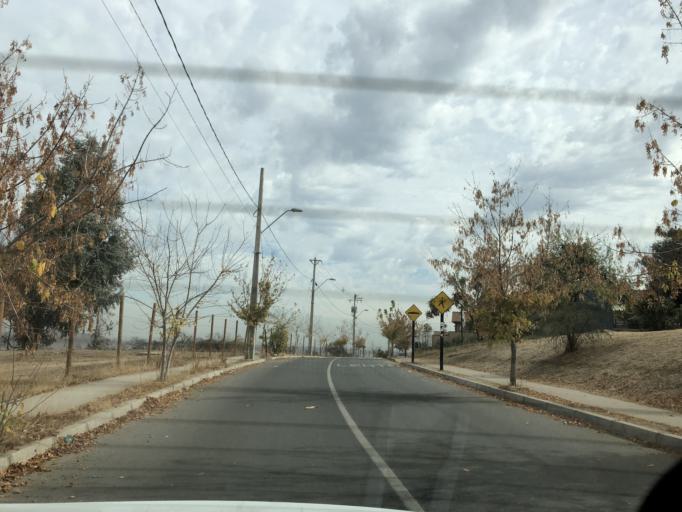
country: CL
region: Santiago Metropolitan
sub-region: Provincia de Cordillera
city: Puente Alto
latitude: -33.5894
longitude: -70.5320
